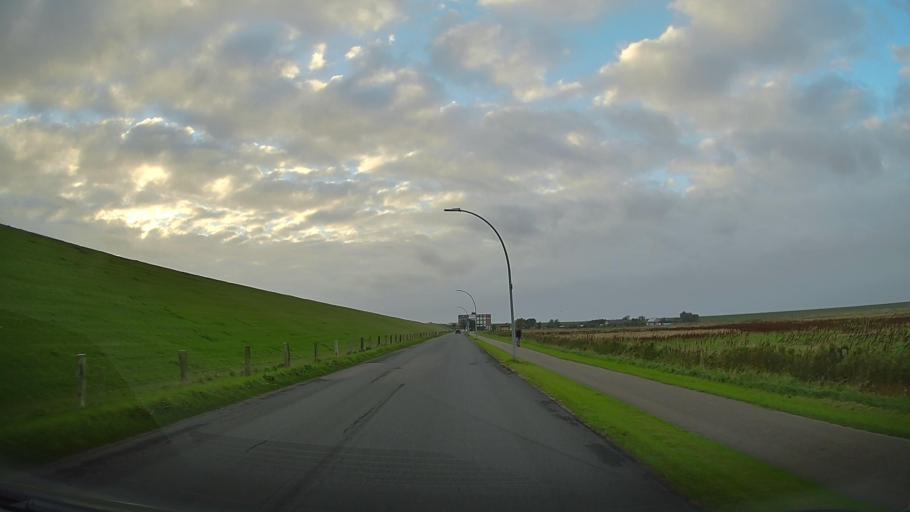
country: DE
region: Schleswig-Holstein
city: Schobull
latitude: 54.4759
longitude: 9.0169
